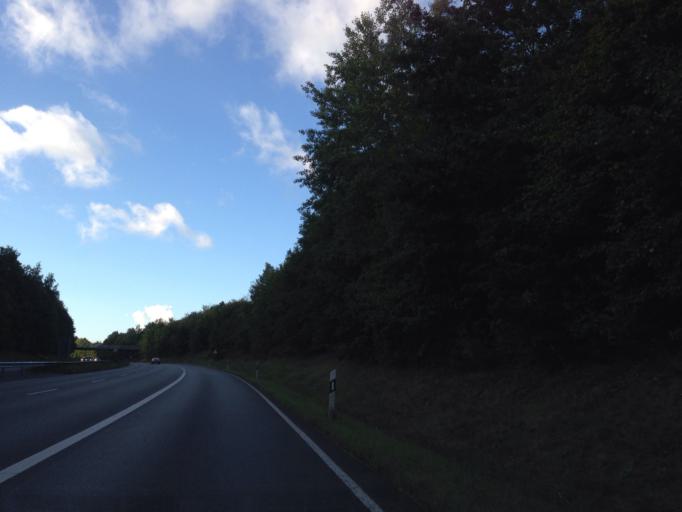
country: DE
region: Lower Saxony
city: Wendisch Evern
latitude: 53.2440
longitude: 10.4549
